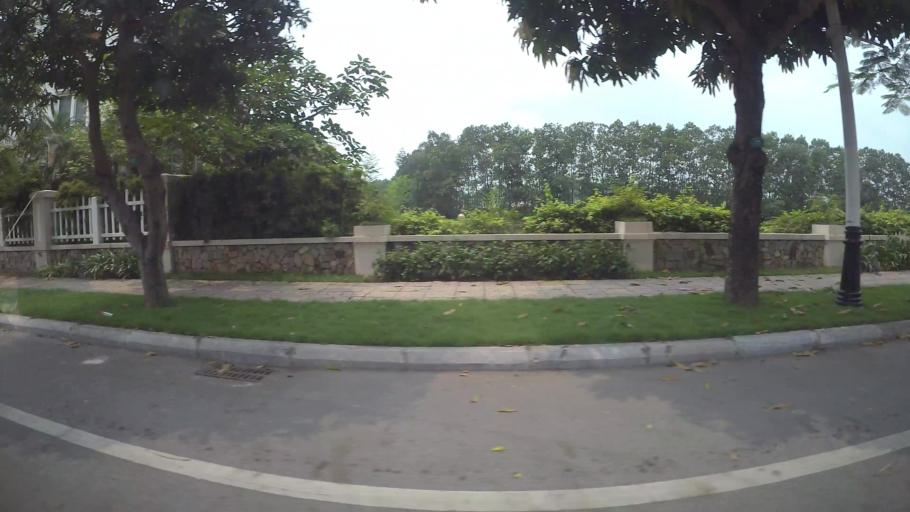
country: VN
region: Ha Noi
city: Trau Quy
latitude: 21.0425
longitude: 105.9159
